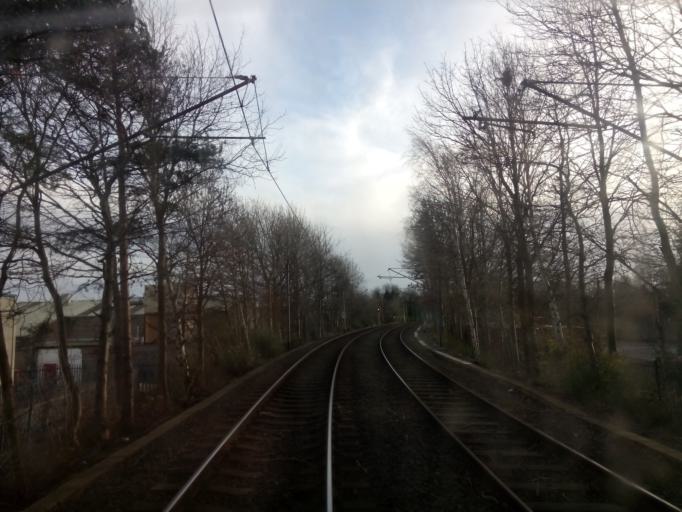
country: GB
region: England
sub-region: Newcastle upon Tyne
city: Gosforth
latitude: 55.0097
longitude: -1.6090
